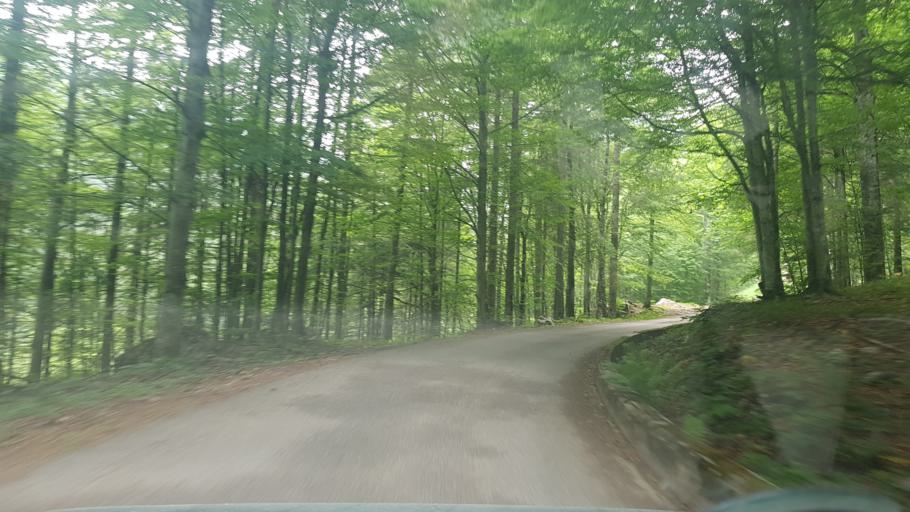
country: IT
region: Friuli Venezia Giulia
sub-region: Provincia di Udine
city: Paularo
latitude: 46.5370
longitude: 13.2059
